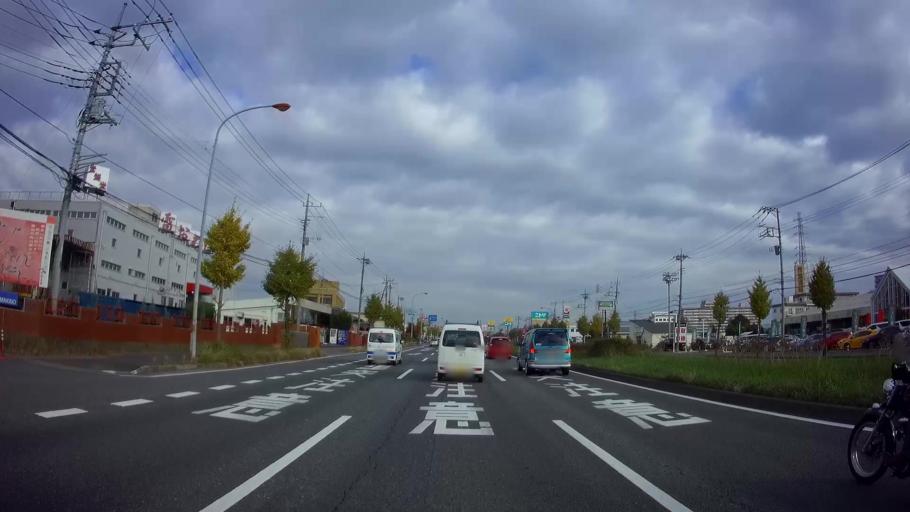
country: JP
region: Saitama
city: Yono
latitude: 35.9163
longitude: 139.5932
